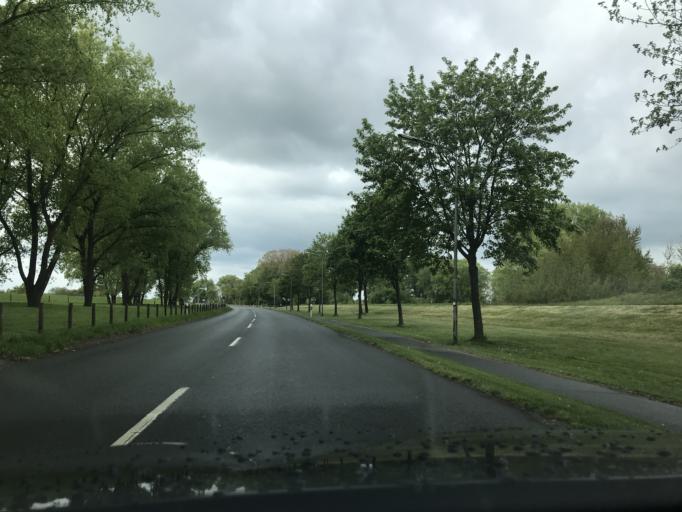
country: DE
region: Lower Saxony
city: Lemwerder
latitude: 53.1684
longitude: 8.5924
